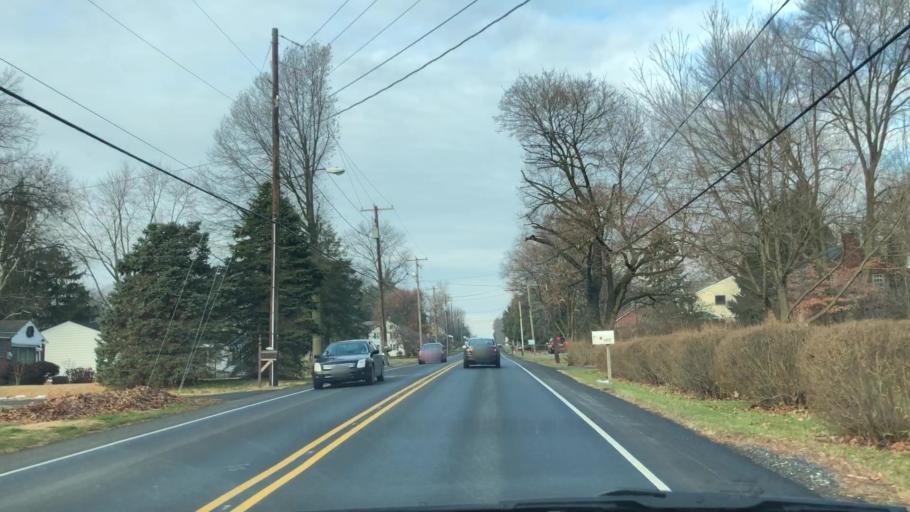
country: US
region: Pennsylvania
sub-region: Lancaster County
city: Landisville
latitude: 40.0563
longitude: -76.3897
